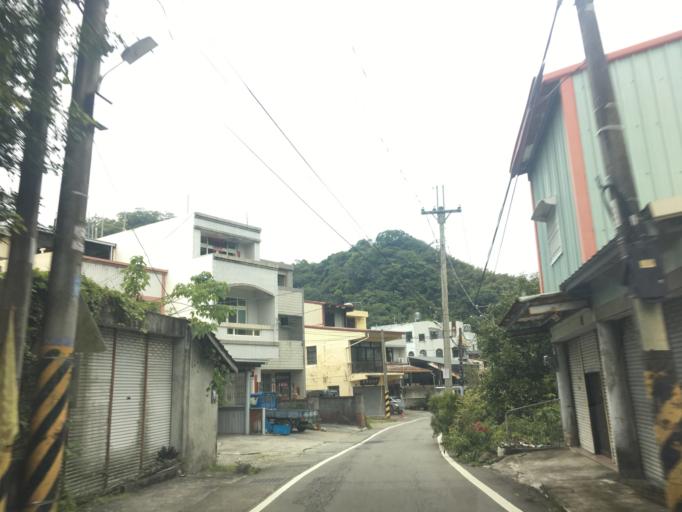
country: TW
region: Taiwan
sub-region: Taichung City
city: Taichung
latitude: 24.1577
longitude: 120.8276
